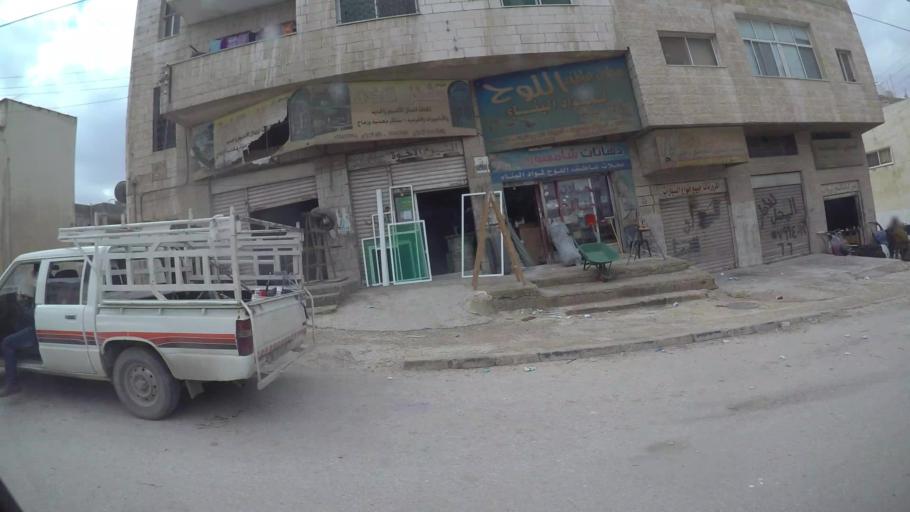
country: JO
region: Amman
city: Al Jubayhah
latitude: 32.0472
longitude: 35.8330
